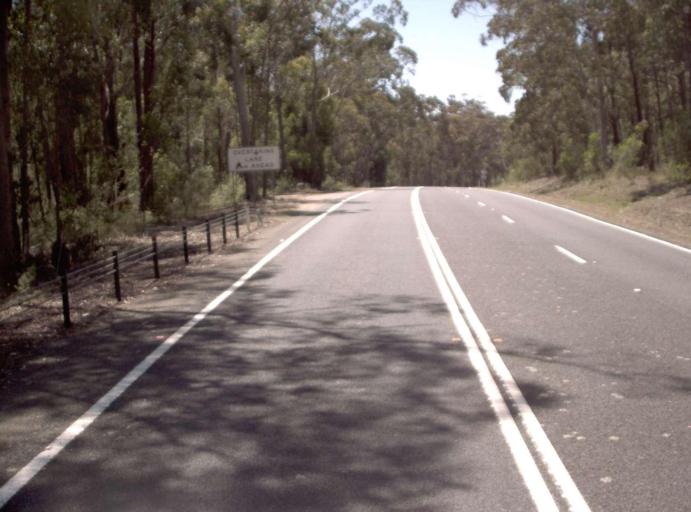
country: AU
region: Victoria
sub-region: East Gippsland
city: Lakes Entrance
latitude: -37.8106
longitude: 148.0303
